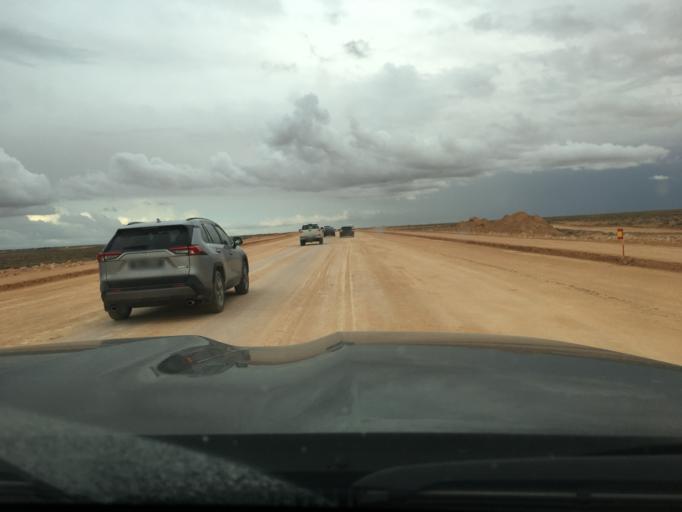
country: TN
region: Madanin
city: Medenine
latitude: 33.2694
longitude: 10.5859
